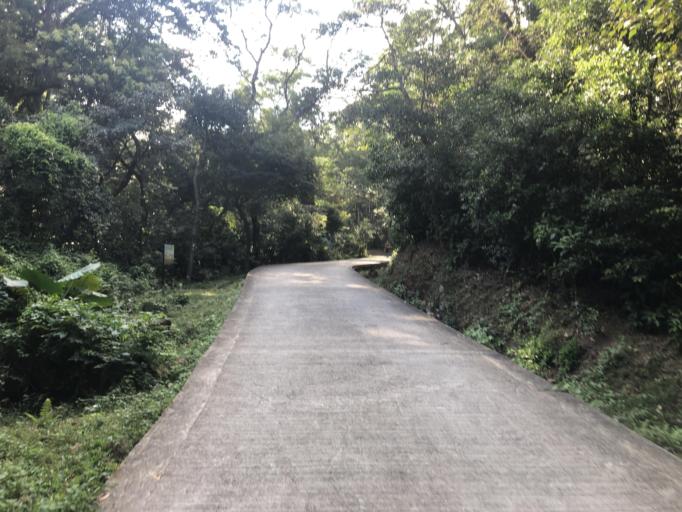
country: HK
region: Tsuen Wan
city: Tsuen Wan
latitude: 22.4075
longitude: 114.1027
